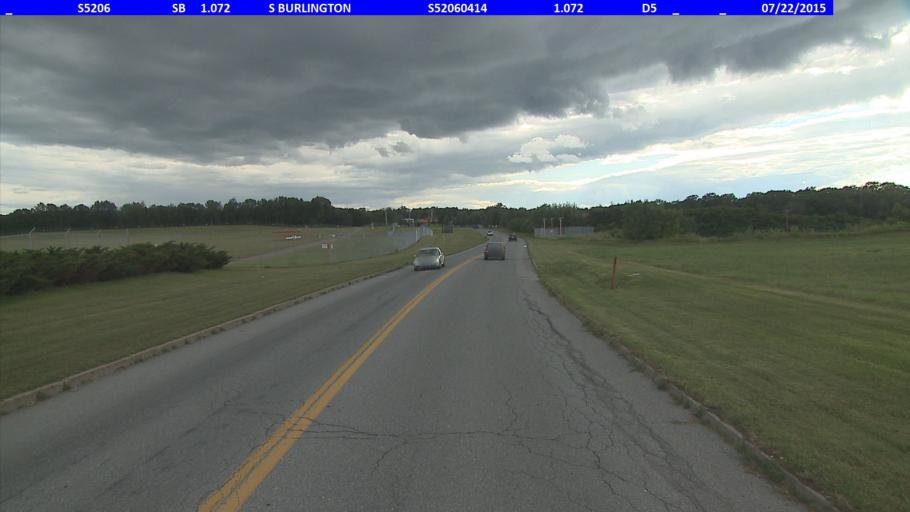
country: US
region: Vermont
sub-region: Chittenden County
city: South Burlington
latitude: 44.4834
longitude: -73.1677
